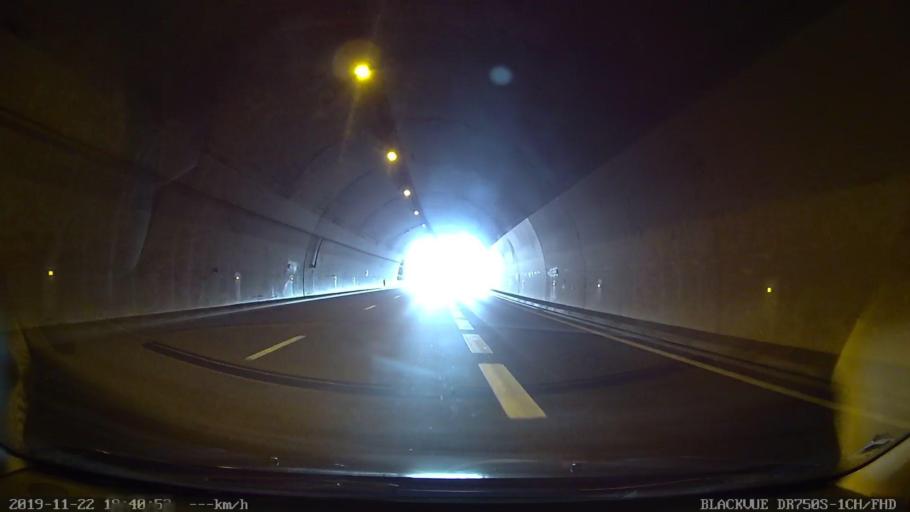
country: RE
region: Reunion
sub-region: Reunion
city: Saint-Paul
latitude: -21.0301
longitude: 55.2535
